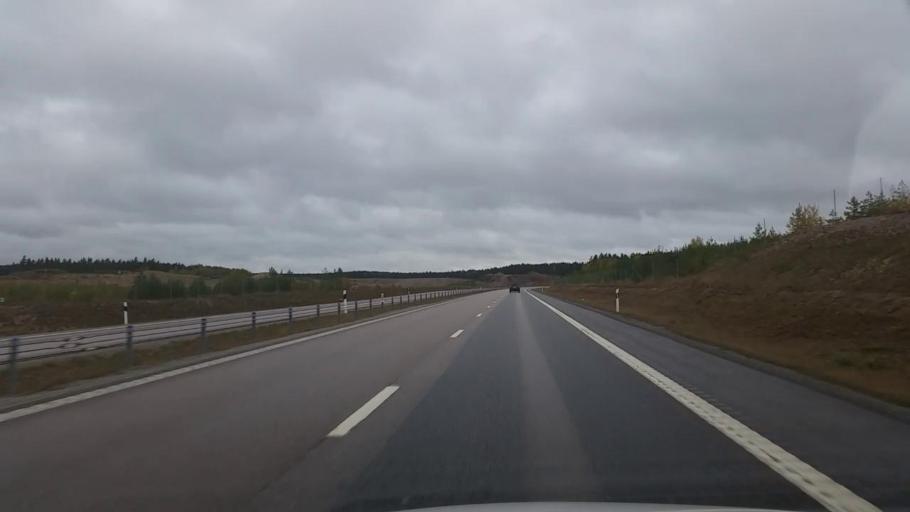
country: SE
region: Uppsala
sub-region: Osthammars Kommun
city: Bjorklinge
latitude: 60.1128
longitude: 17.5535
